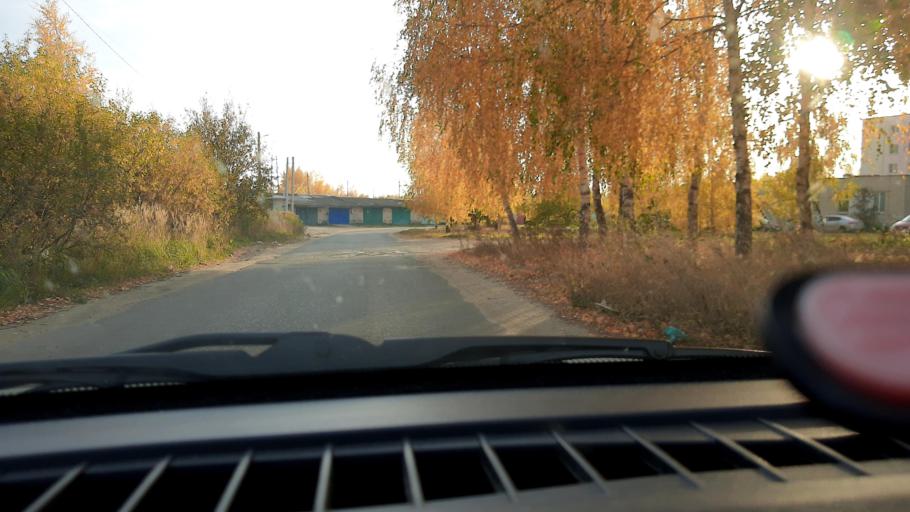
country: RU
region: Nizjnij Novgorod
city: Gorodets
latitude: 56.6377
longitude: 43.4876
